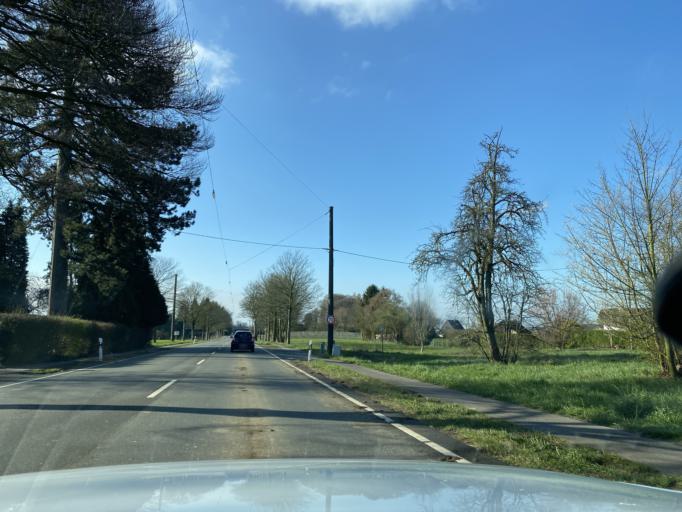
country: DE
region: North Rhine-Westphalia
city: Burscheid
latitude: 51.0791
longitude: 7.1301
